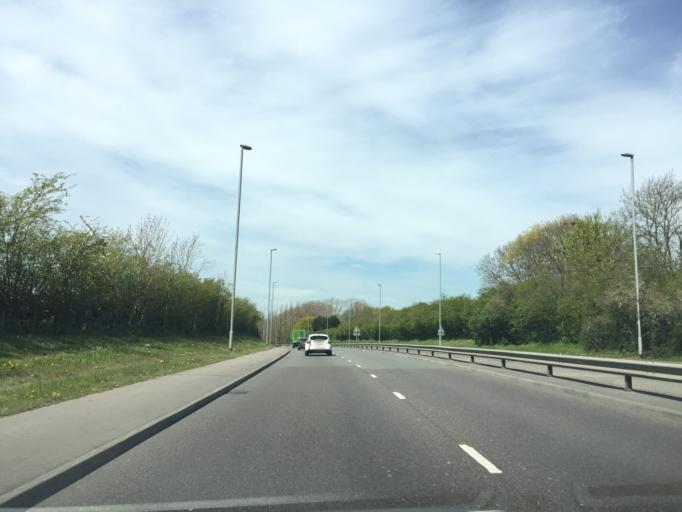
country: GB
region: England
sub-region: Essex
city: Harlow
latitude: 51.7508
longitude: 0.1333
